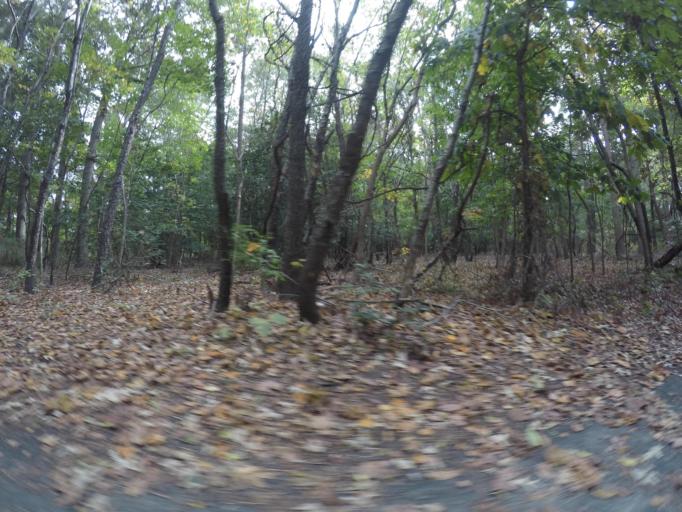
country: US
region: Delaware
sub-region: Sussex County
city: Rehoboth Beach
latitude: 38.7205
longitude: -75.1057
